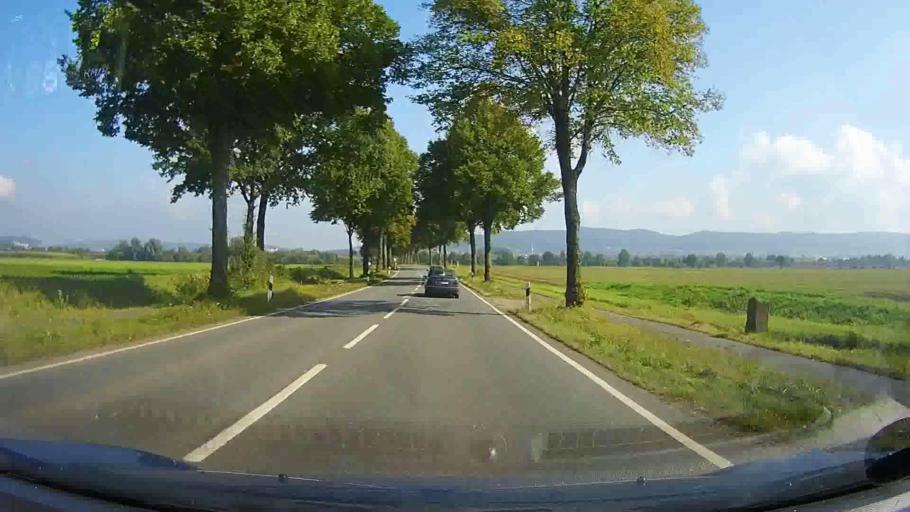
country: DE
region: Lower Saxony
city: Hillerse
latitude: 51.7048
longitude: 9.9699
